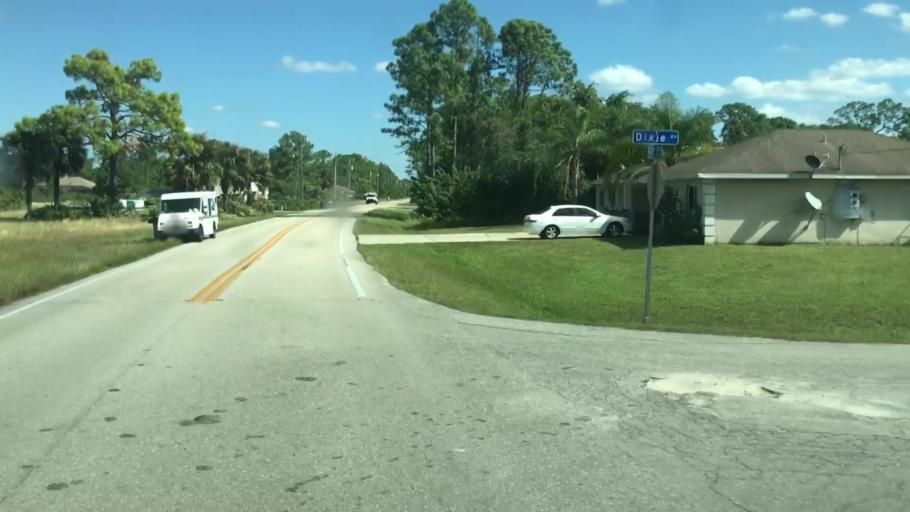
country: US
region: Florida
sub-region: Lee County
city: Lehigh Acres
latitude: 26.6426
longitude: -81.6580
